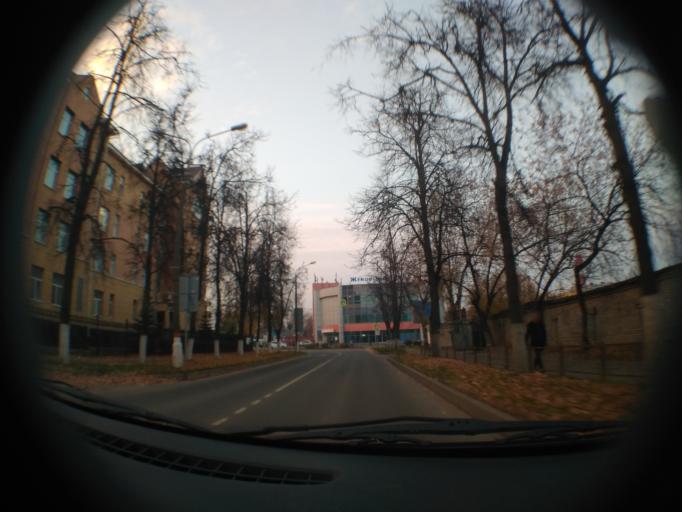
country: RU
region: Moskovskaya
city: Zhukovskiy
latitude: 55.6007
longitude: 38.1154
